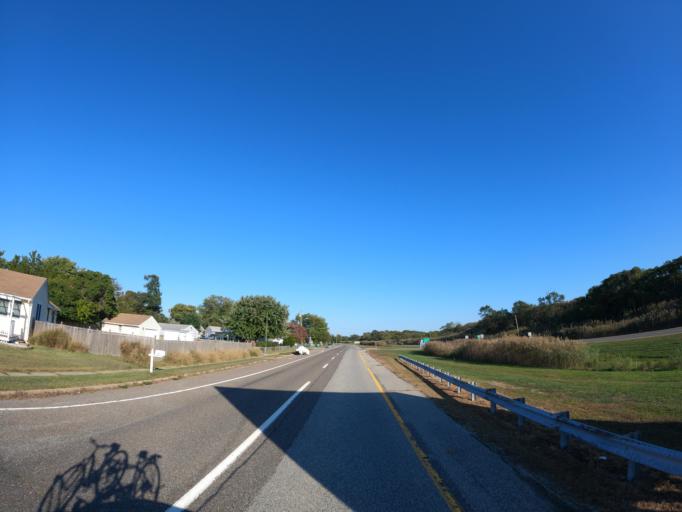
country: US
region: New Jersey
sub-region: Cape May County
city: North Cape May
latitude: 38.9737
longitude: -74.9558
